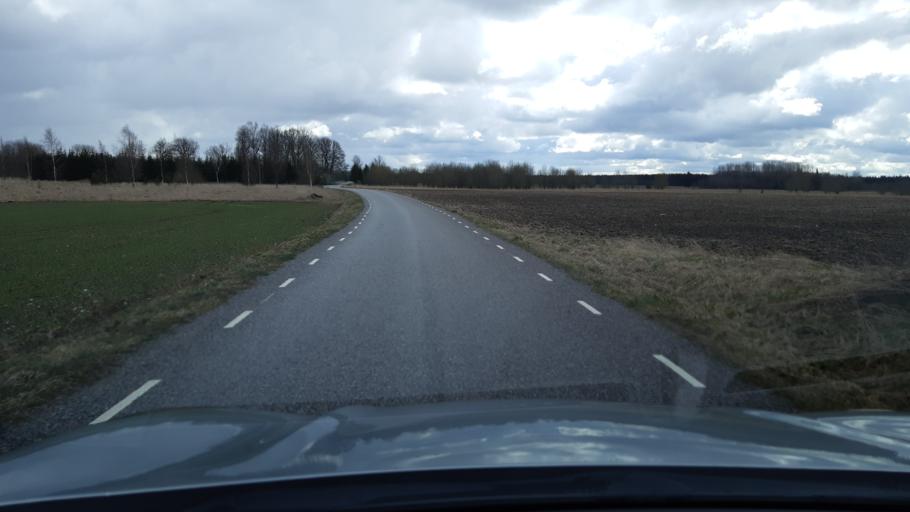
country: EE
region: Raplamaa
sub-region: Rapla vald
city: Rapla
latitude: 59.0642
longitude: 24.7594
